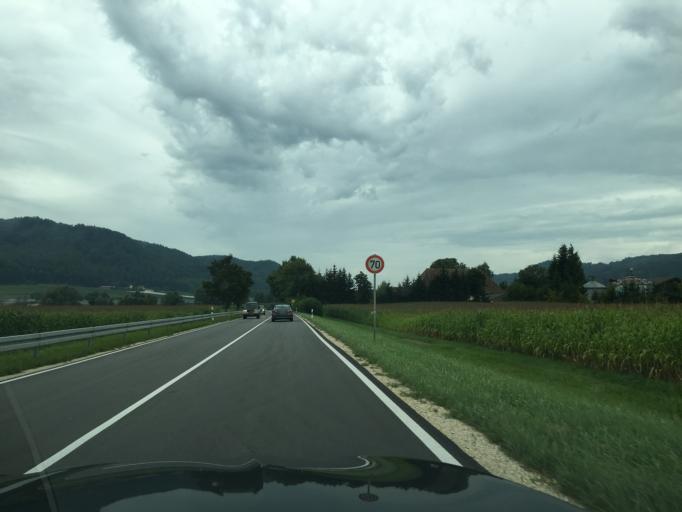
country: DE
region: Baden-Wuerttemberg
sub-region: Freiburg Region
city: Stockach
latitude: 47.8117
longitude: 8.9918
